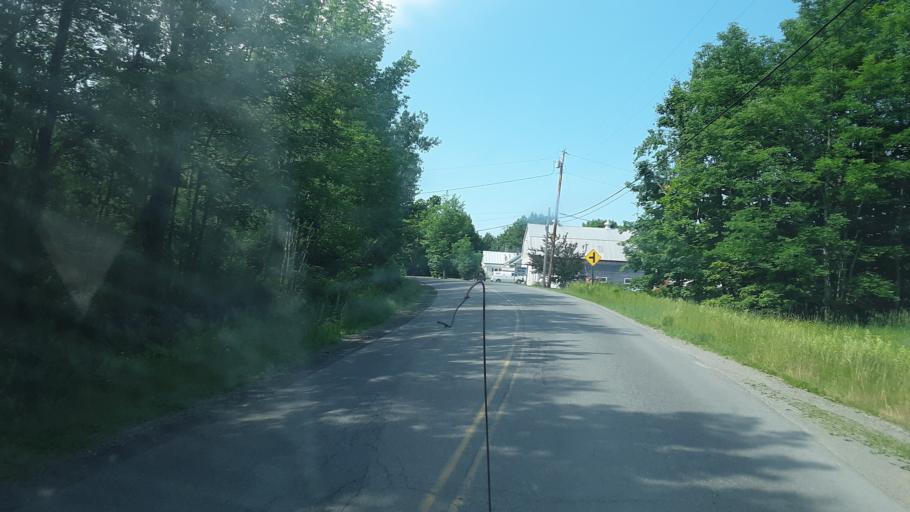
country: US
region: Maine
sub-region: Waldo County
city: Swanville
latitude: 44.5407
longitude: -68.9837
